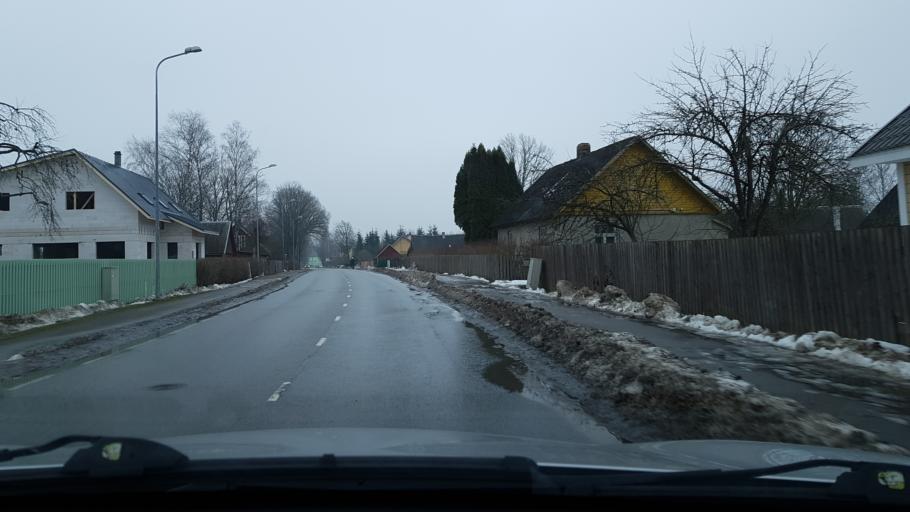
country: EE
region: Valgamaa
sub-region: Torva linn
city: Torva
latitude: 58.2345
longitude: 25.8728
